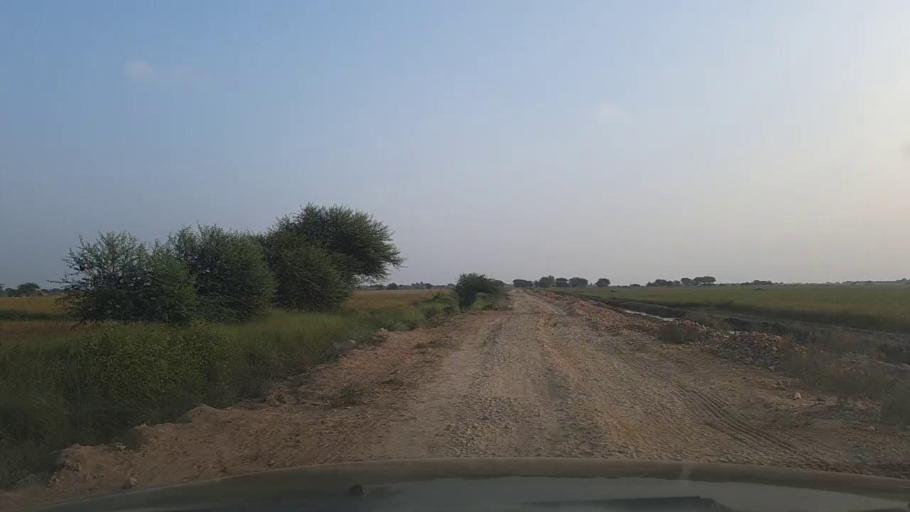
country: PK
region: Sindh
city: Jati
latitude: 24.5409
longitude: 68.3597
